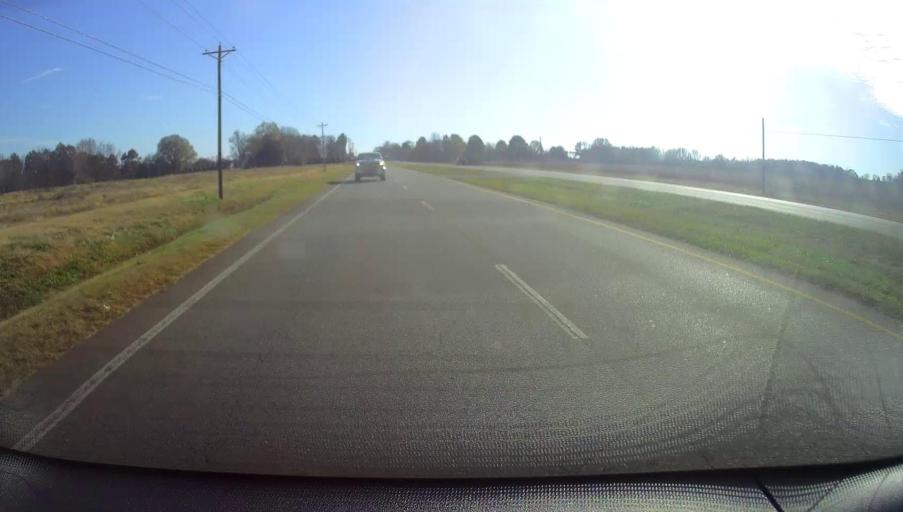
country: US
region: Alabama
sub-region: Limestone County
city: Athens
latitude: 34.7672
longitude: -86.9572
